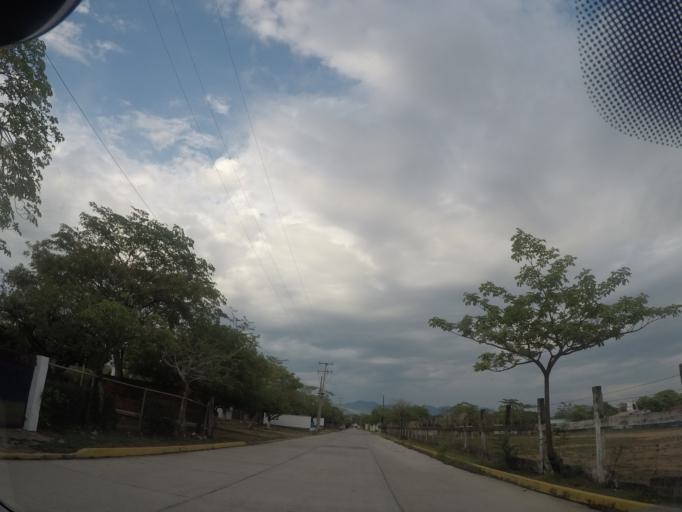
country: MX
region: Oaxaca
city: Chahuite
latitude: 16.3042
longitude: -94.1933
